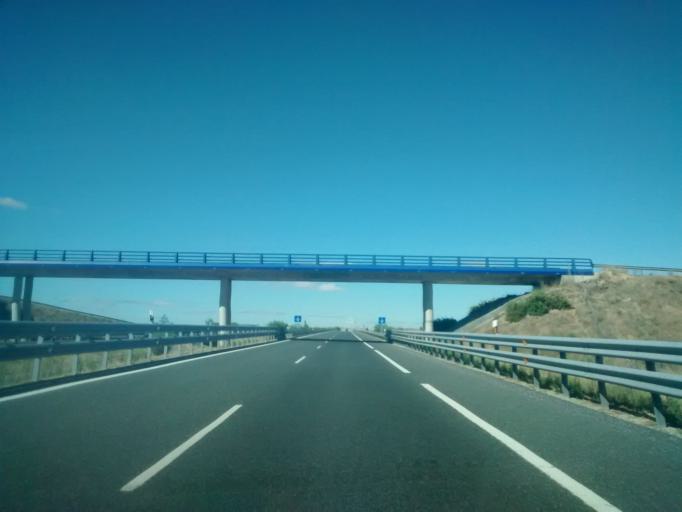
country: ES
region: Castille and Leon
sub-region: Provincia de Avila
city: Narros del Castillo
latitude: 40.8814
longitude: -5.0439
